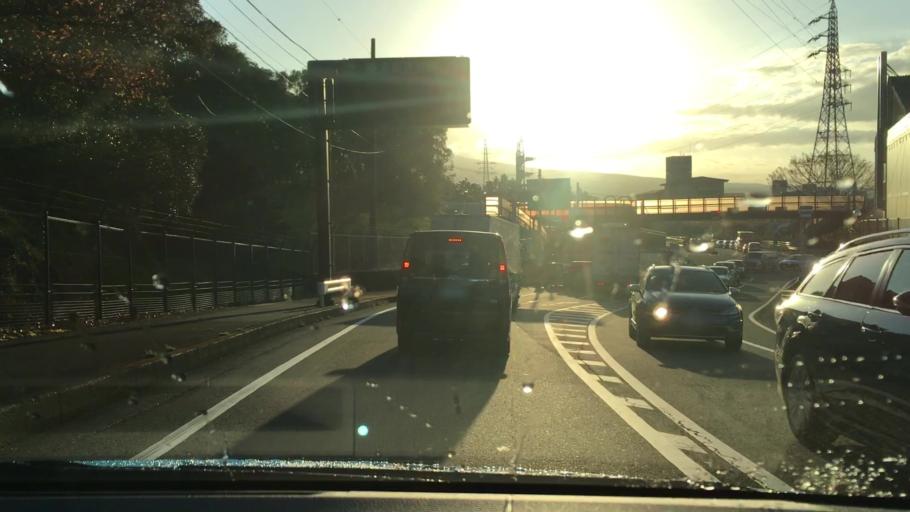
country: JP
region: Shizuoka
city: Gotemba
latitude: 35.2206
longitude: 138.9063
